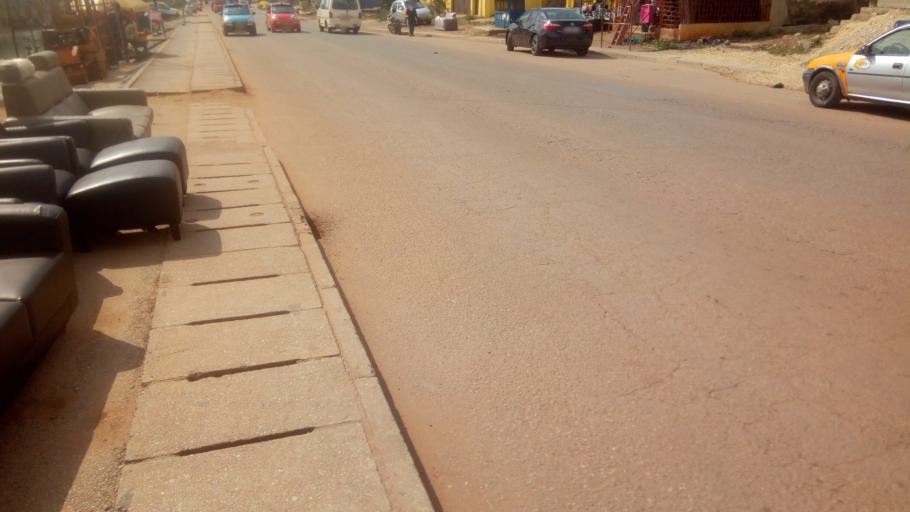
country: GH
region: Ashanti
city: Obuasi
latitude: 6.2099
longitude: -1.6849
